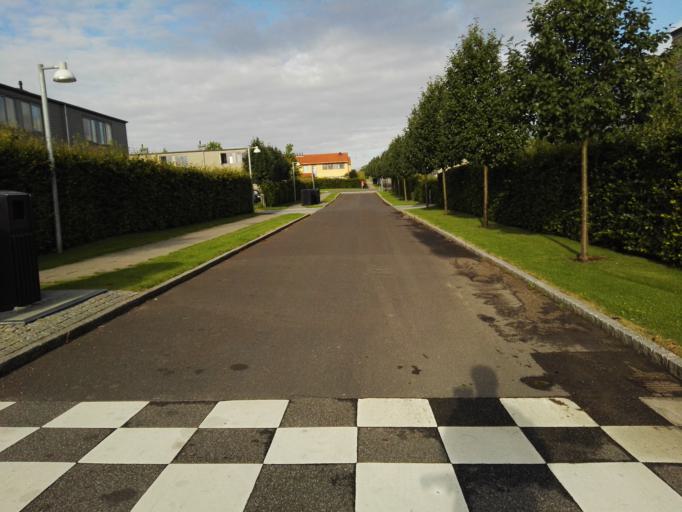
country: DK
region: Capital Region
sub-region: Ballerup Kommune
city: Malov
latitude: 55.7446
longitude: 12.3191
